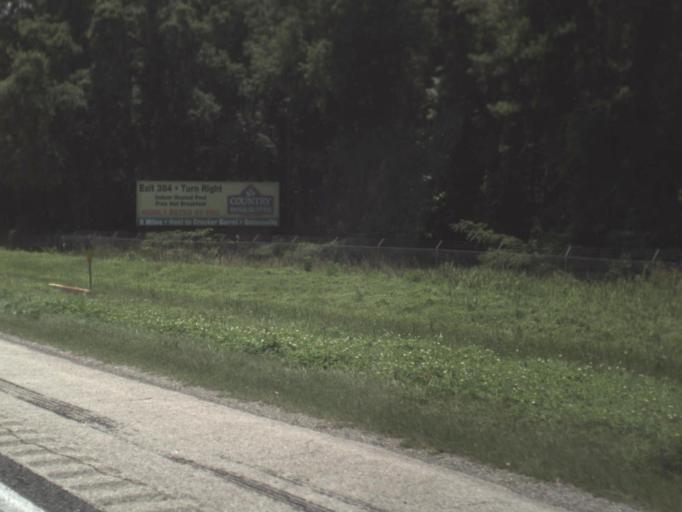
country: US
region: Florida
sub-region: Alachua County
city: Alachua
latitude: 29.6776
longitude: -82.4358
